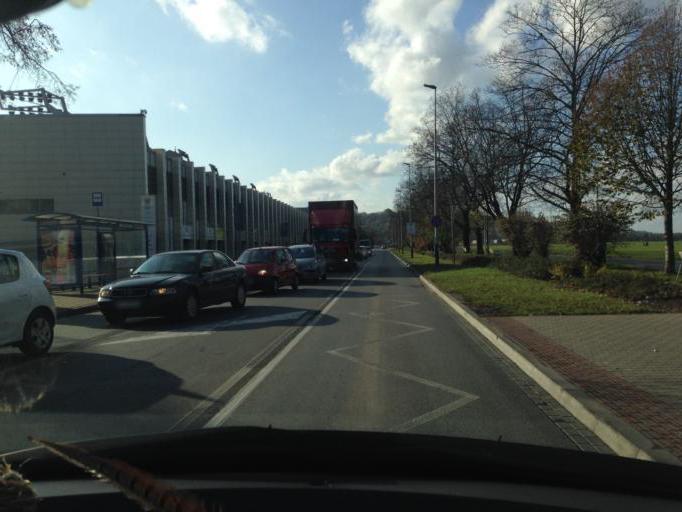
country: PL
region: Lesser Poland Voivodeship
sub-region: Krakow
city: Krakow
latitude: 50.0589
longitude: 19.9220
